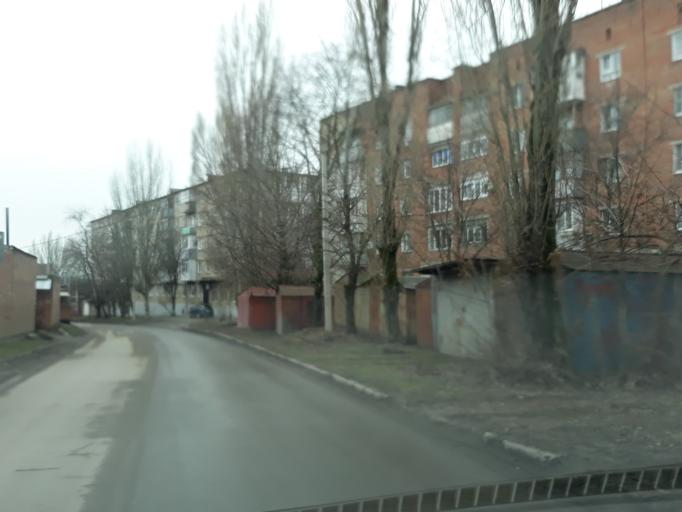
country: RU
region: Rostov
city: Taganrog
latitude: 47.2076
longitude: 38.8987
